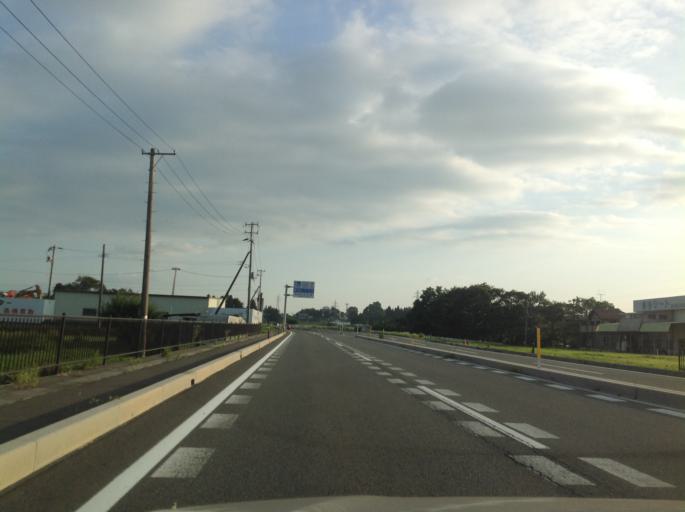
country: JP
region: Iwate
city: Hanamaki
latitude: 39.5017
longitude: 141.1455
